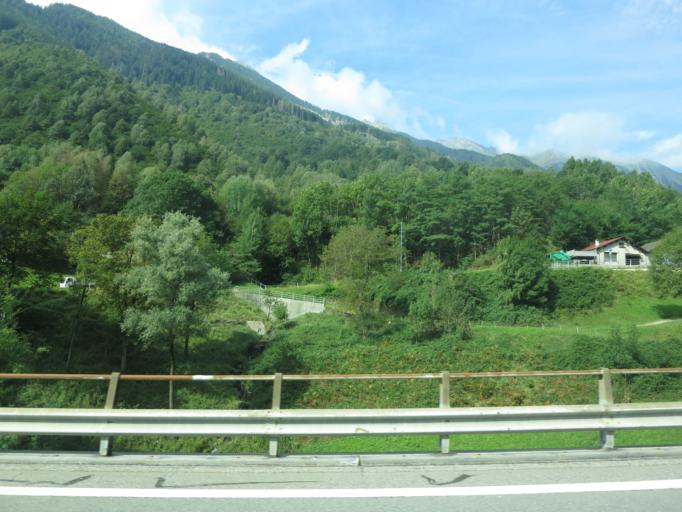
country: CH
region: Grisons
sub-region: Moesa District
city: Mesocco
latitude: 46.3844
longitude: 9.2338
